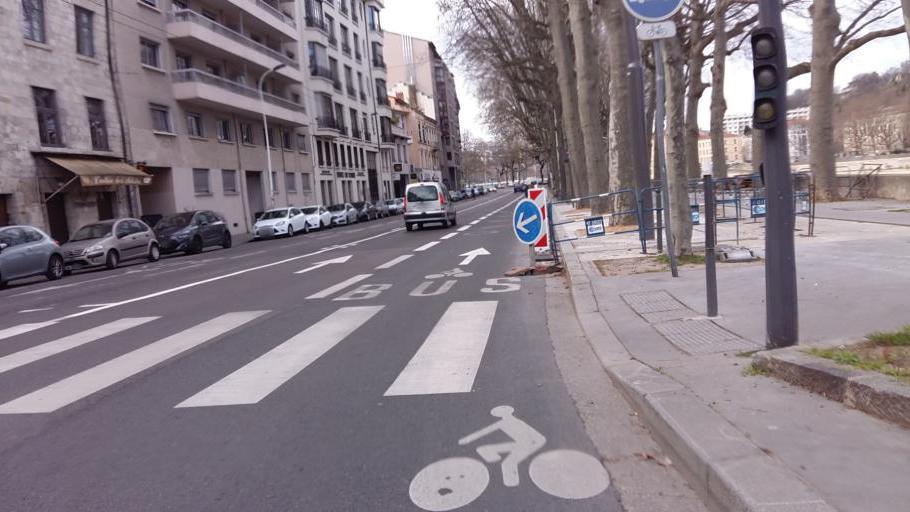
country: FR
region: Rhone-Alpes
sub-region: Departement du Rhone
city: Tassin-la-Demi-Lune
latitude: 45.7702
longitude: 4.8124
